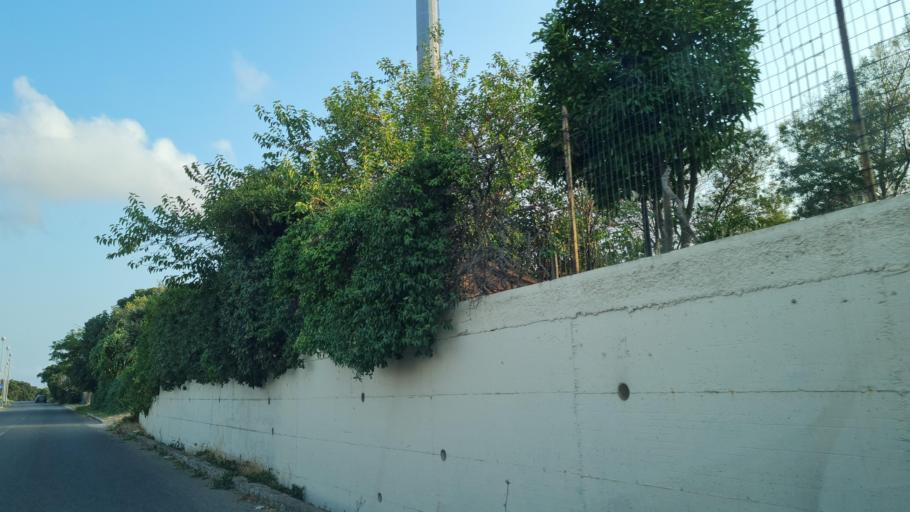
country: IT
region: Latium
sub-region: Provincia di Viterbo
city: Montalto di Castro
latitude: 42.3449
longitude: 11.6096
